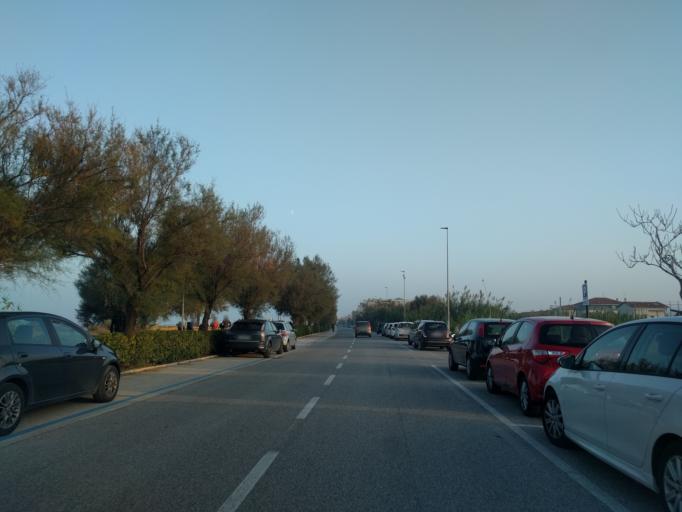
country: IT
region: The Marches
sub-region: Provincia di Ancona
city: Senigallia
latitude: 43.7411
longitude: 13.1854
